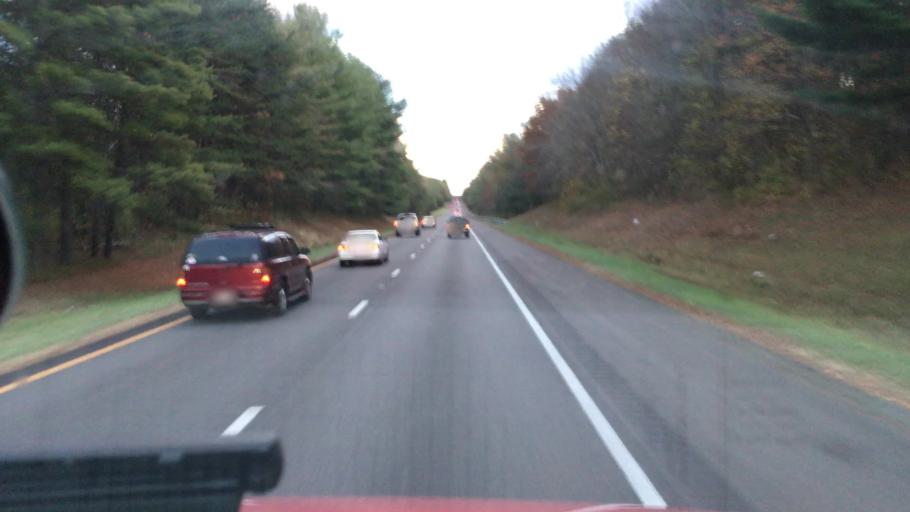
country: US
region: Virginia
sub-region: Fluvanna County
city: Palmyra
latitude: 37.9574
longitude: -78.1603
